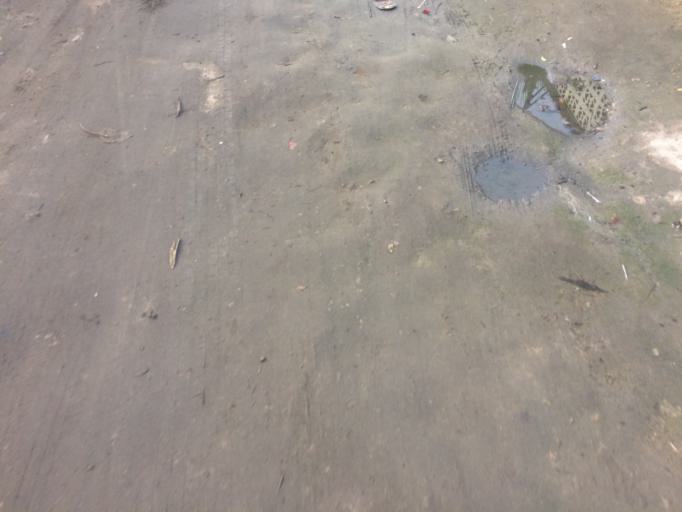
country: TZ
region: Dar es Salaam
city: Magomeni
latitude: -6.7874
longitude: 39.2576
